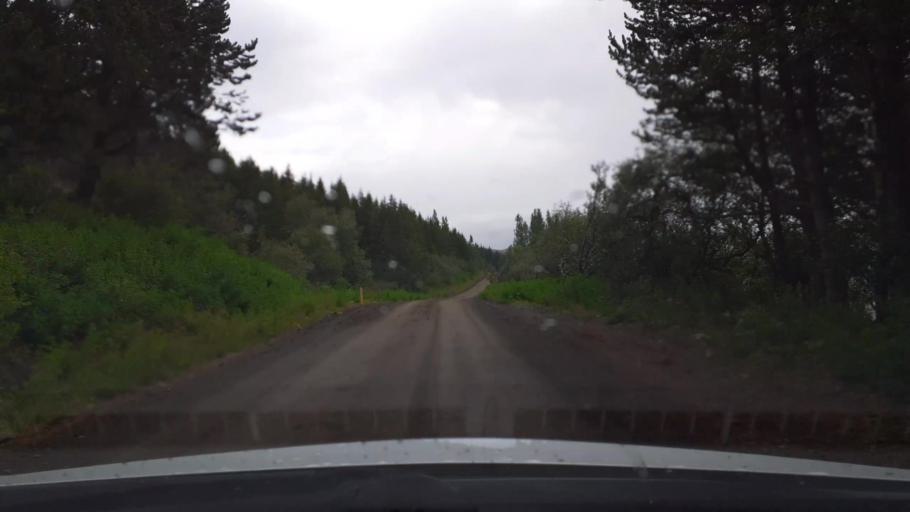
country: IS
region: Capital Region
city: Mosfellsbaer
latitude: 64.5176
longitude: -21.4228
